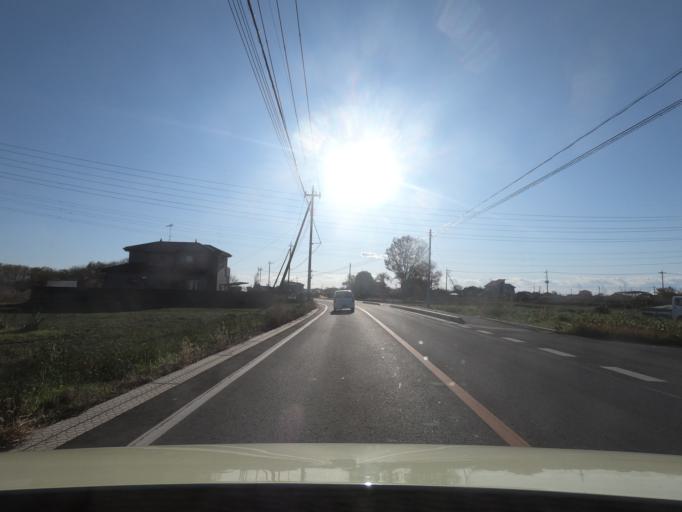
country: JP
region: Tochigi
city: Fujioka
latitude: 36.2755
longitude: 139.6793
